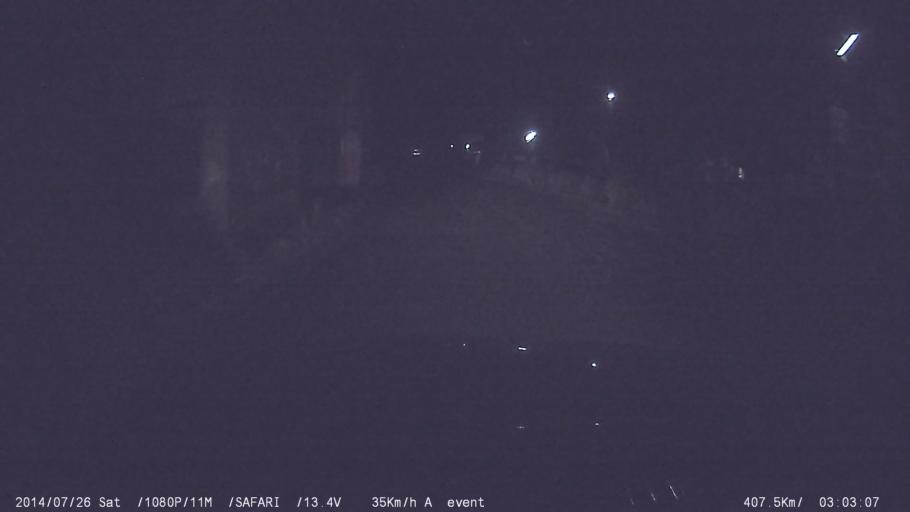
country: IN
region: Kerala
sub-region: Palakkad district
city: Palakkad
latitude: 10.7159
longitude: 76.5974
